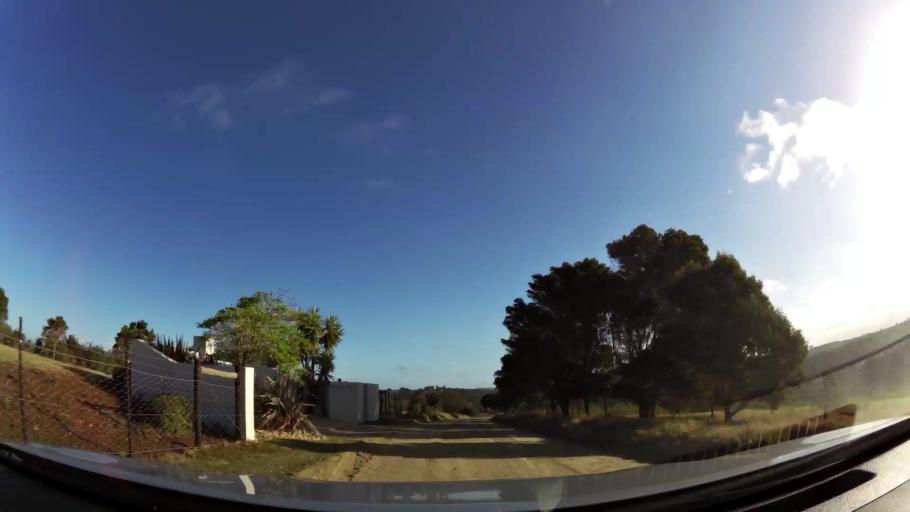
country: ZA
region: Western Cape
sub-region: Eden District Municipality
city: George
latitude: -33.9887
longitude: 22.5657
